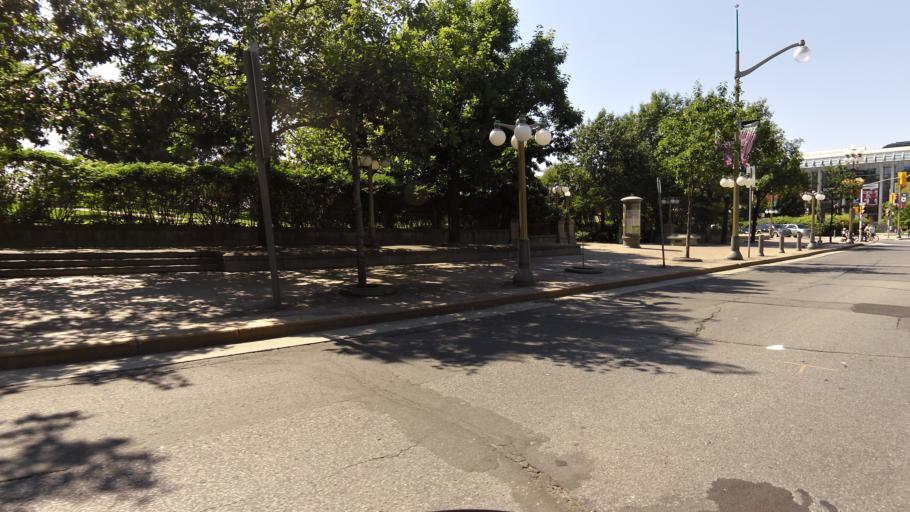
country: CA
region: Ontario
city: Ottawa
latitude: 45.4281
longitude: -75.6966
